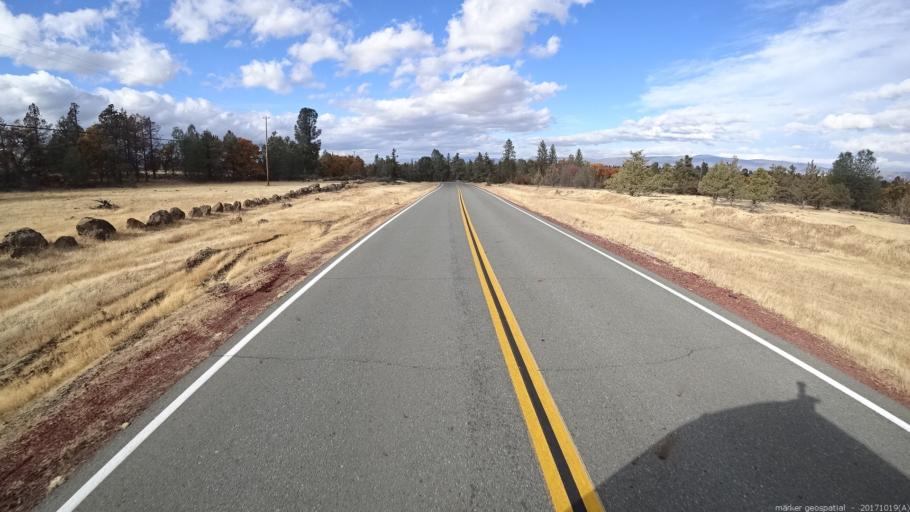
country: US
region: California
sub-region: Shasta County
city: Burney
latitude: 40.9922
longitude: -121.4300
